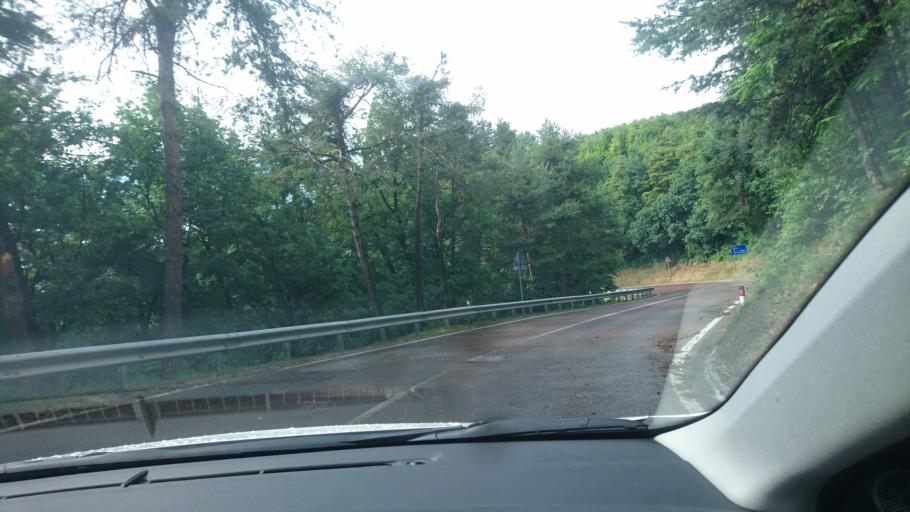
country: IT
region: Trentino-Alto Adige
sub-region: Provincia di Trento
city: Sanzeno
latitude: 46.3705
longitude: 11.0852
